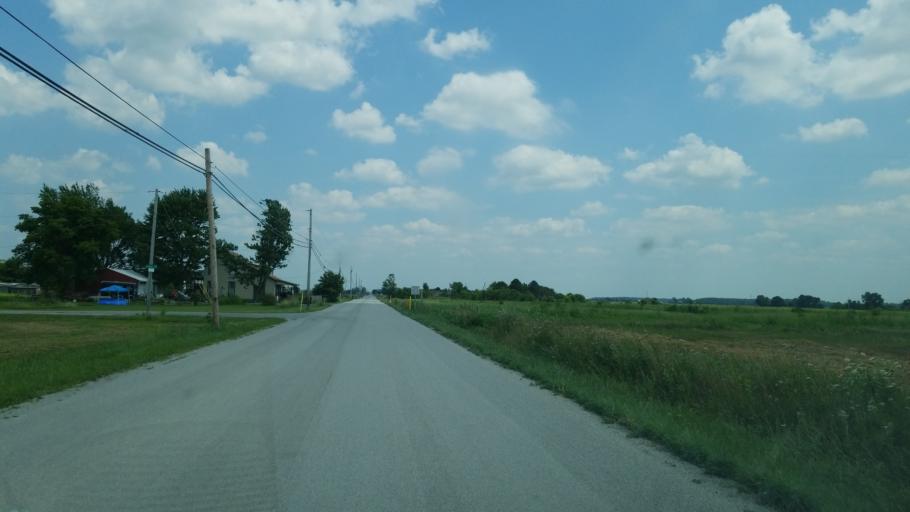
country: US
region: Ohio
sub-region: Wood County
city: North Baltimore
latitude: 41.2401
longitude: -83.6074
